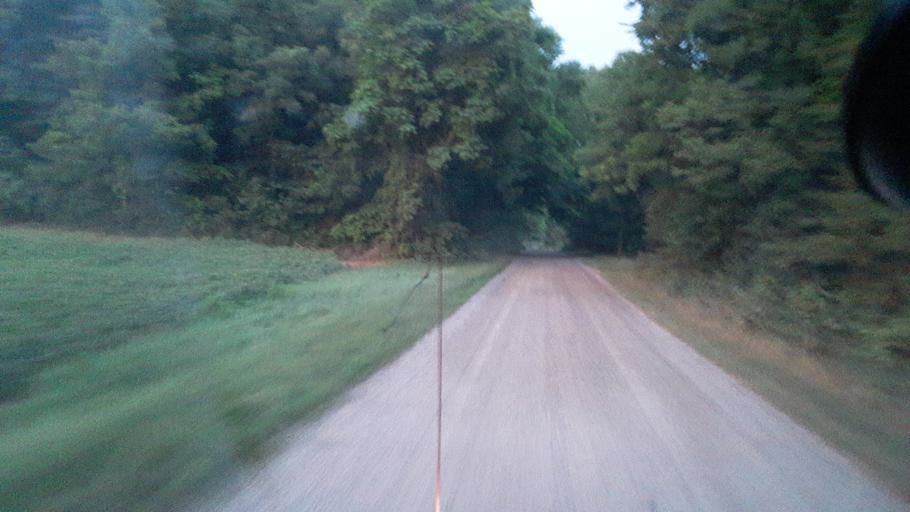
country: US
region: Indiana
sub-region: DeKalb County
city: Butler
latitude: 41.3618
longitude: -84.8249
